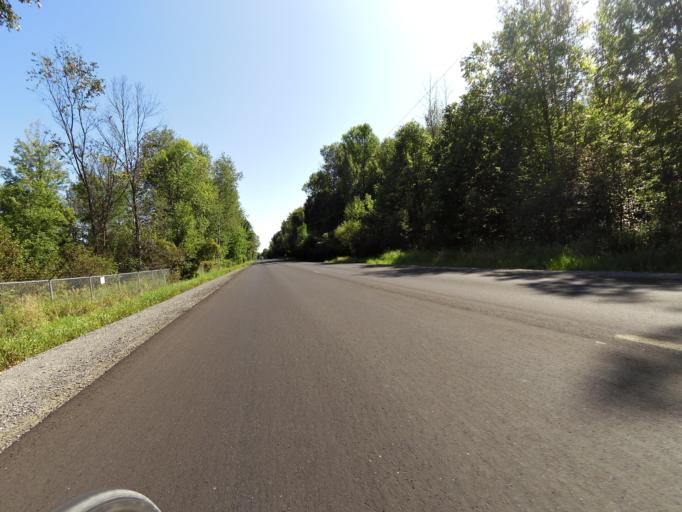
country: CA
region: Ontario
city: Bells Corners
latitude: 45.3793
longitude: -75.9399
